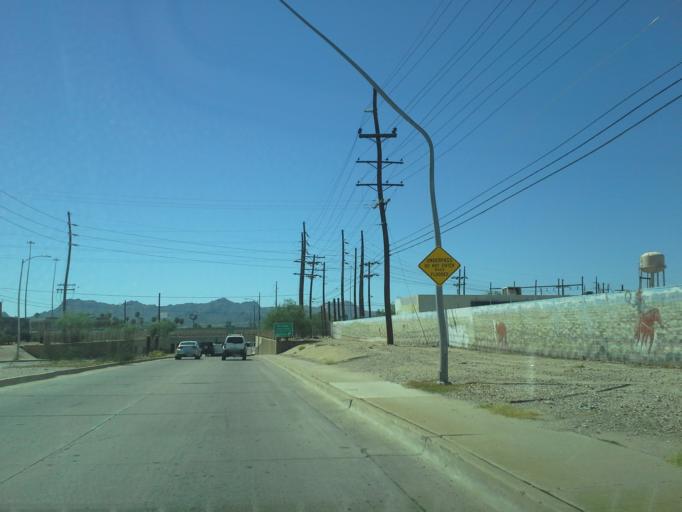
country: US
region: Arizona
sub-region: Pima County
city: Flowing Wells
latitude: 32.2504
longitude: -110.9894
